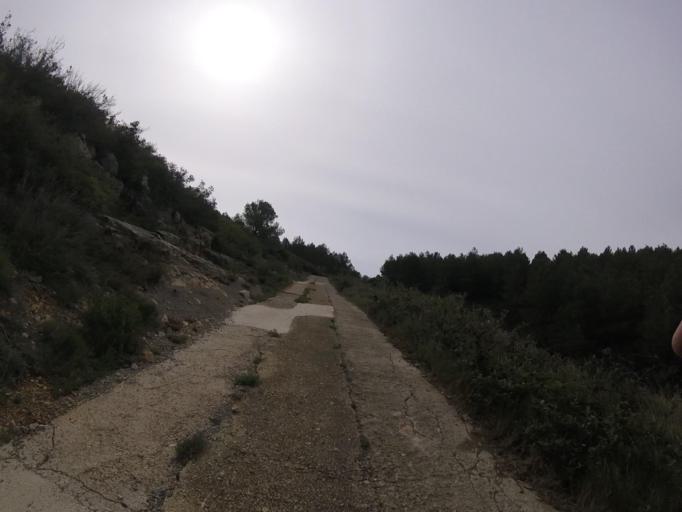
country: ES
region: Valencia
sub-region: Provincia de Castello
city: Cabanes
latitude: 40.1894
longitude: 0.0795
